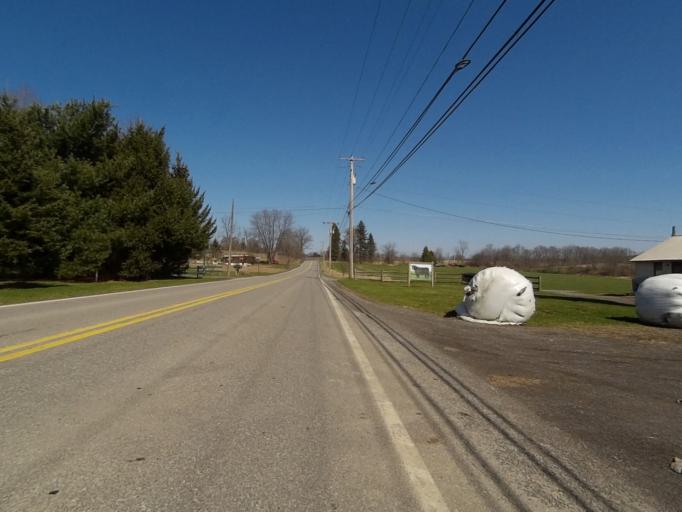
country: US
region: Pennsylvania
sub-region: Centre County
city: Stormstown
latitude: 40.7825
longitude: -78.0336
